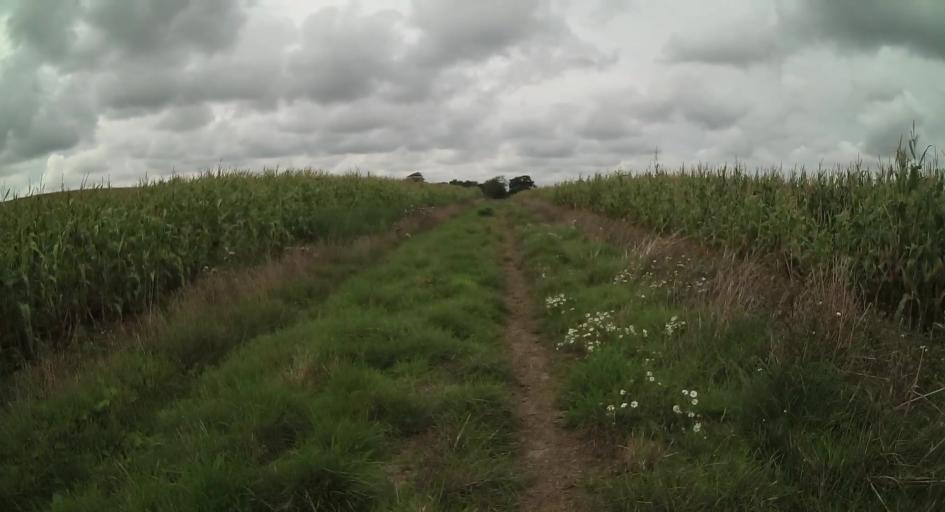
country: GB
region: England
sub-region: Isle of Wight
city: Newport
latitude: 50.6618
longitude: -1.2650
